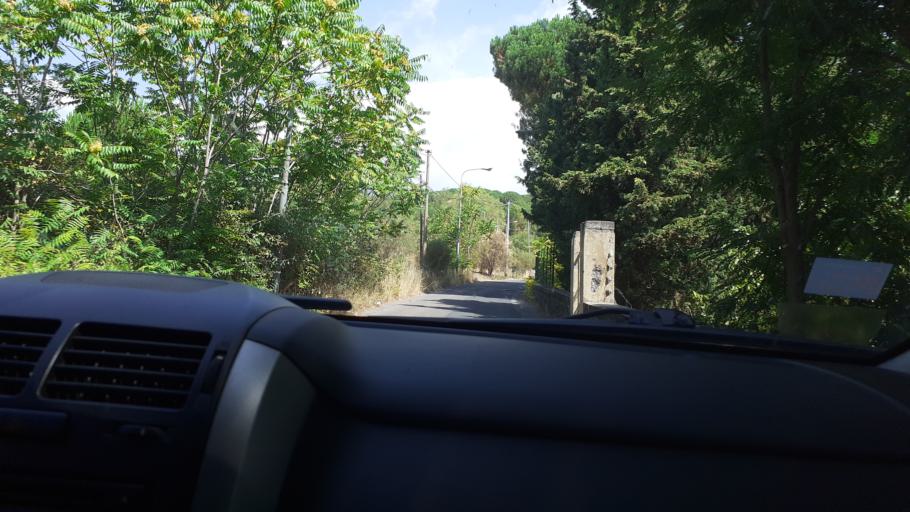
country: IT
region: Sicily
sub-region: Catania
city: Nicolosi
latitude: 37.6263
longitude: 15.0246
